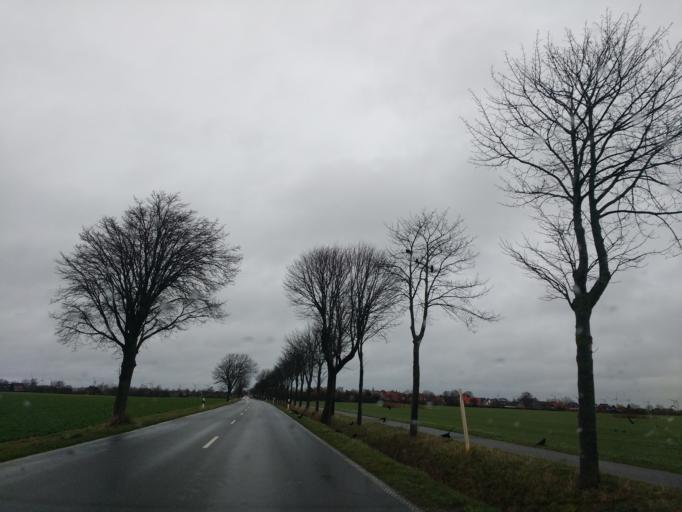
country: DE
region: Schleswig-Holstein
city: Fehmarn
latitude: 54.4516
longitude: 11.2053
